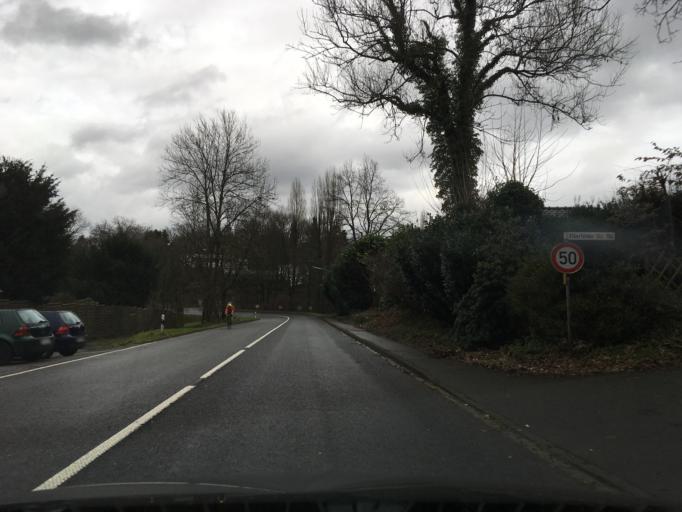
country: DE
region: North Rhine-Westphalia
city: Haan
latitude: 51.2108
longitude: 7.0373
